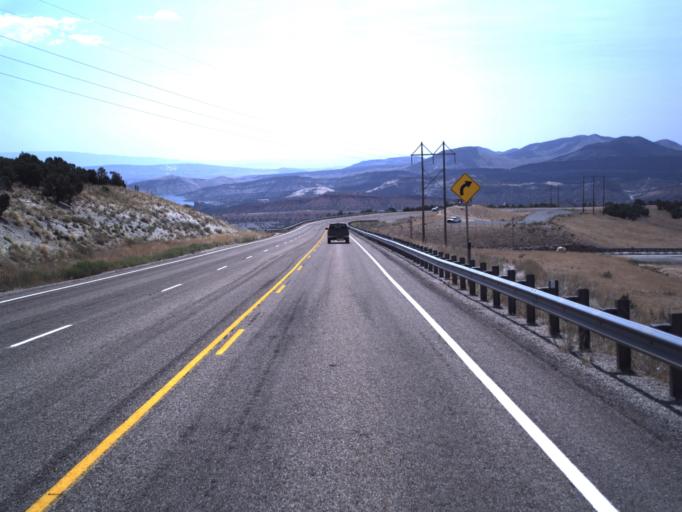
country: US
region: Utah
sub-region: Uintah County
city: Vernal
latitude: 40.6259
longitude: -109.4746
